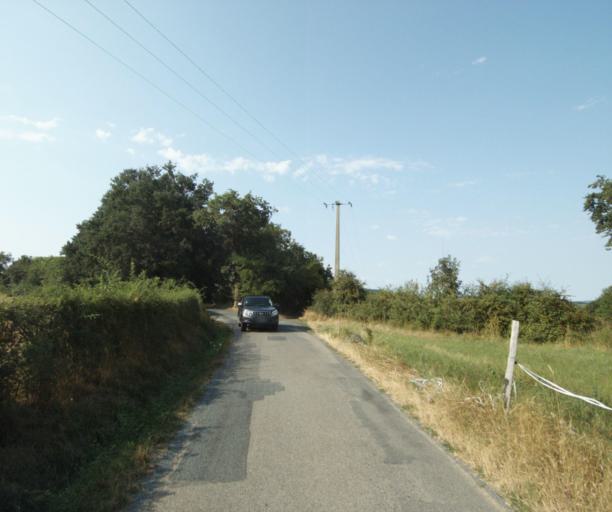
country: FR
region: Rhone-Alpes
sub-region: Departement du Rhone
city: Savigny
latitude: 45.8326
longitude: 4.5751
